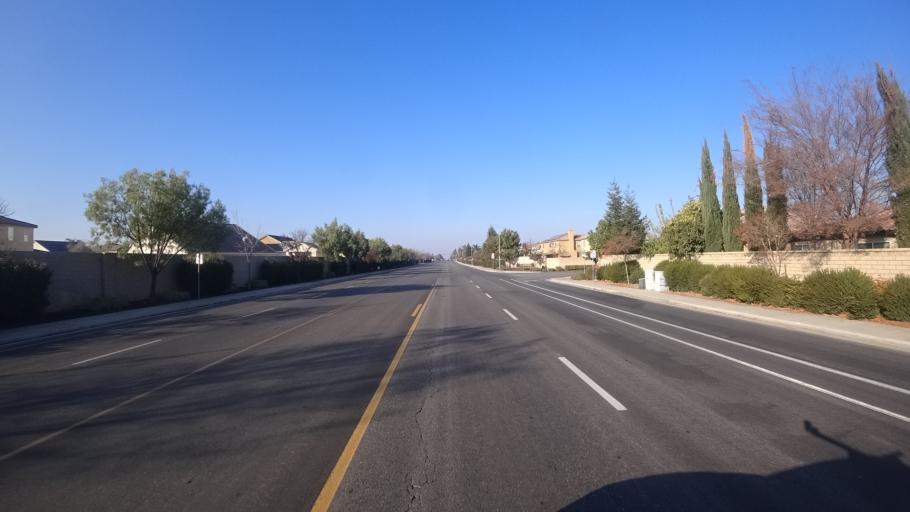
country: US
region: California
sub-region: Kern County
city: Greenacres
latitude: 35.3035
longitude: -119.1144
